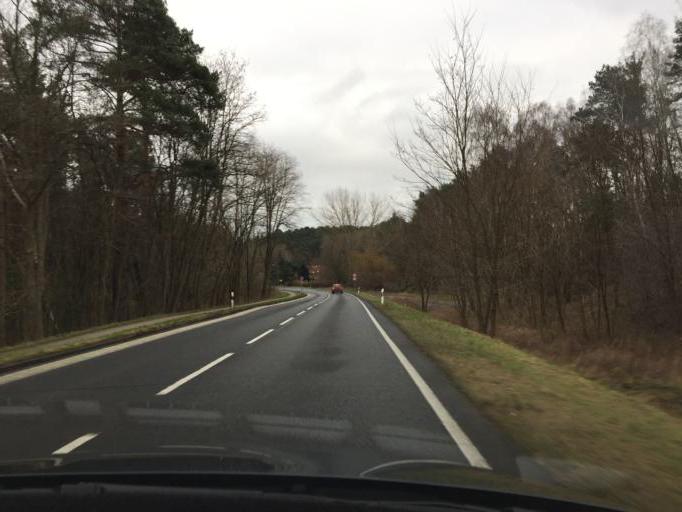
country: DE
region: Brandenburg
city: Eisenhuettenstadt
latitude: 52.1511
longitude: 14.5966
